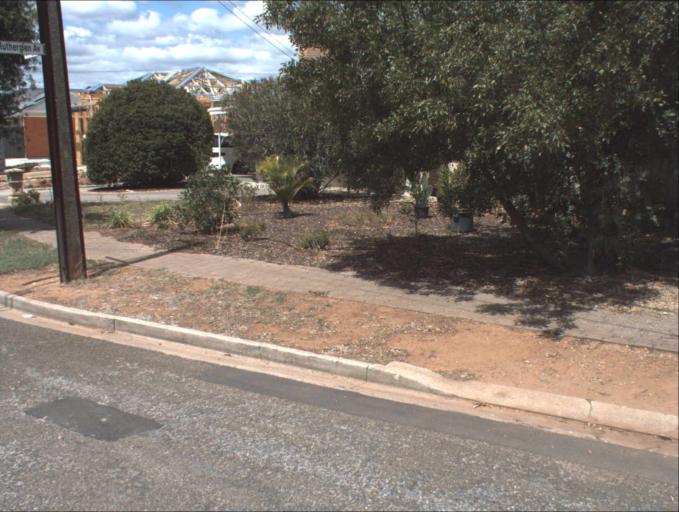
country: AU
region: South Australia
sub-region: Port Adelaide Enfield
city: Gilles Plains
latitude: -34.8449
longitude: 138.6561
